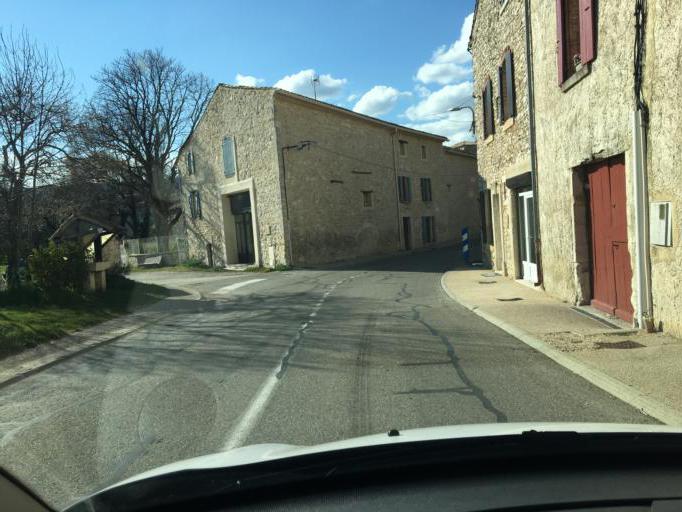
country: FR
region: Provence-Alpes-Cote d'Azur
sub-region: Departement du Vaucluse
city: Sault
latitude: 44.0930
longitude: 5.3998
